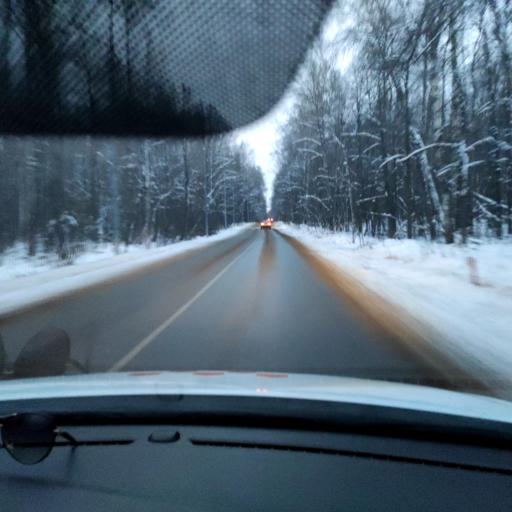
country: RU
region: Tatarstan
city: Vysokaya Gora
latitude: 55.9346
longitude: 49.1778
